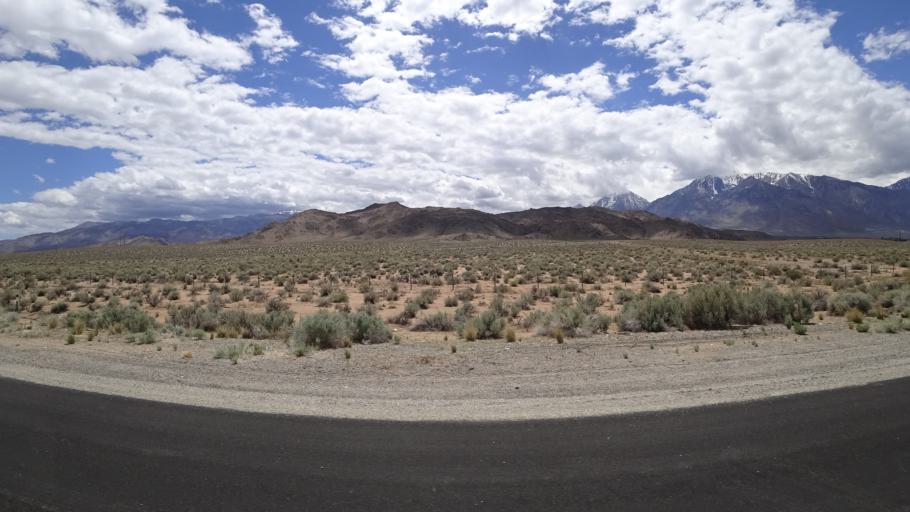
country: US
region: California
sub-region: Inyo County
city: West Bishop
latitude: 37.3967
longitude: -118.5200
